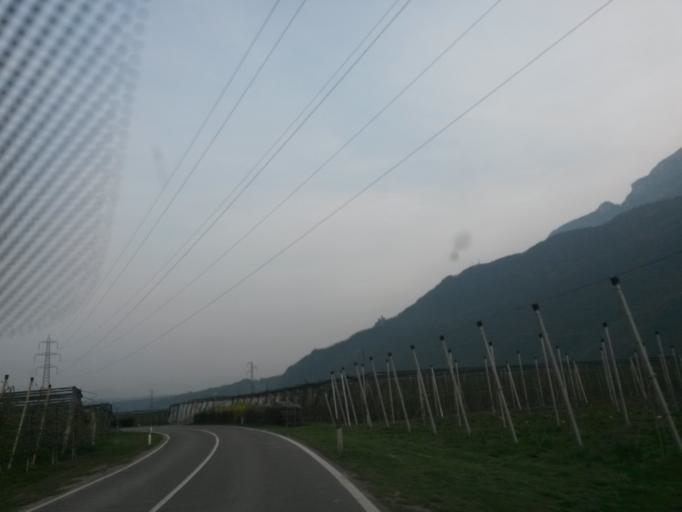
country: IT
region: Trentino-Alto Adige
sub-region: Bolzano
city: Andriano
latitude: 46.5186
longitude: 11.2450
